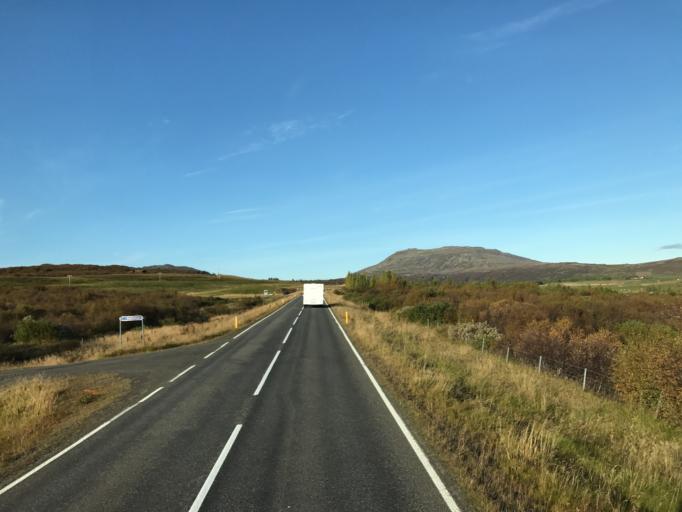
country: IS
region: South
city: Selfoss
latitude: 64.2626
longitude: -20.4700
